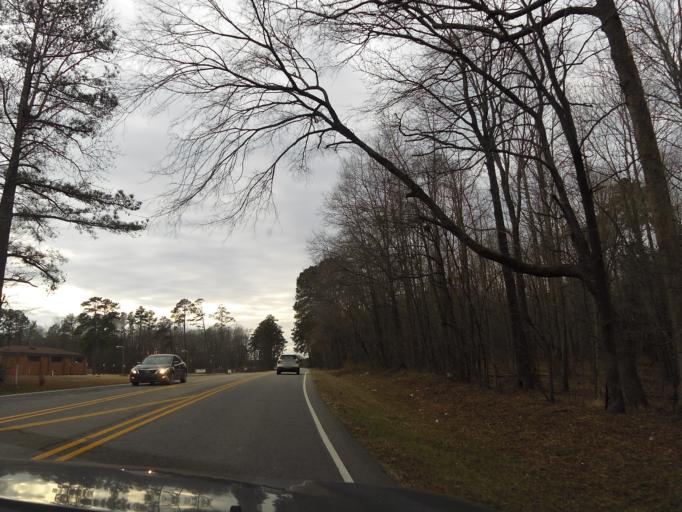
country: US
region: North Carolina
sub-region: Edgecombe County
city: Tarboro
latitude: 35.9783
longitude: -77.6023
